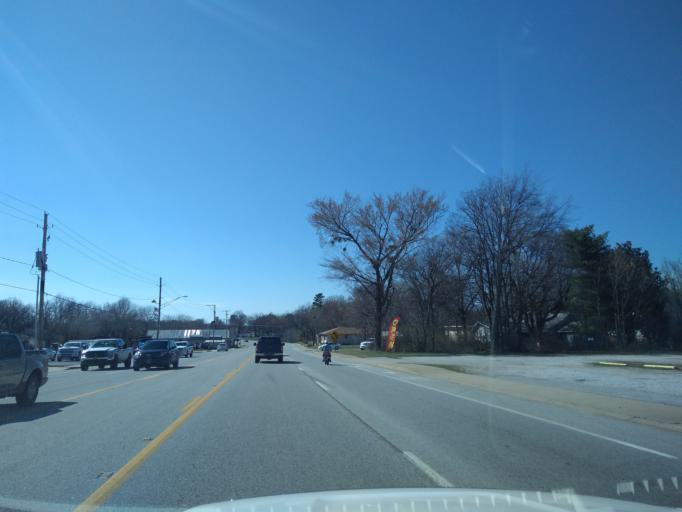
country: US
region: Arkansas
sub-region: Washington County
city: Farmington
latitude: 36.0420
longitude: -94.2447
